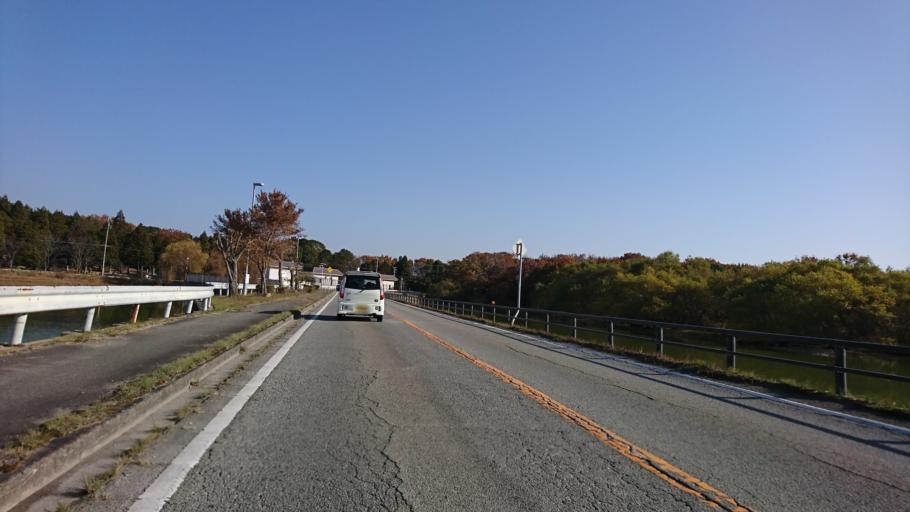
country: JP
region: Hyogo
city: Miki
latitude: 34.7605
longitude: 134.9443
